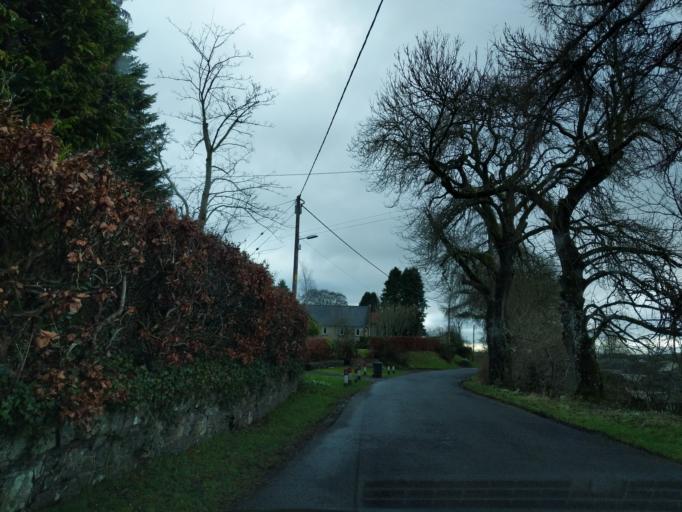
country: GB
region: Scotland
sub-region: Dumfries and Galloway
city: Moffat
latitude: 55.3260
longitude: -3.4307
